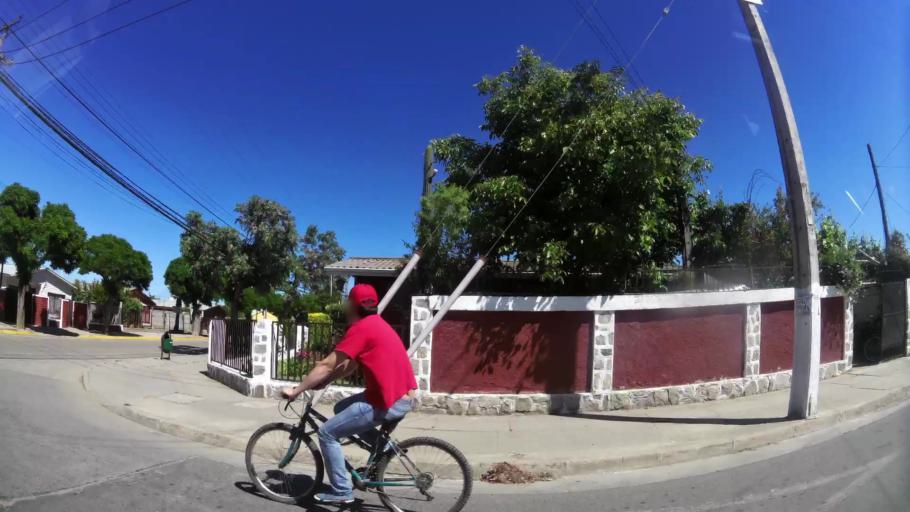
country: CL
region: Valparaiso
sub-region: Provincia de Marga Marga
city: Quilpue
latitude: -33.3204
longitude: -71.4043
